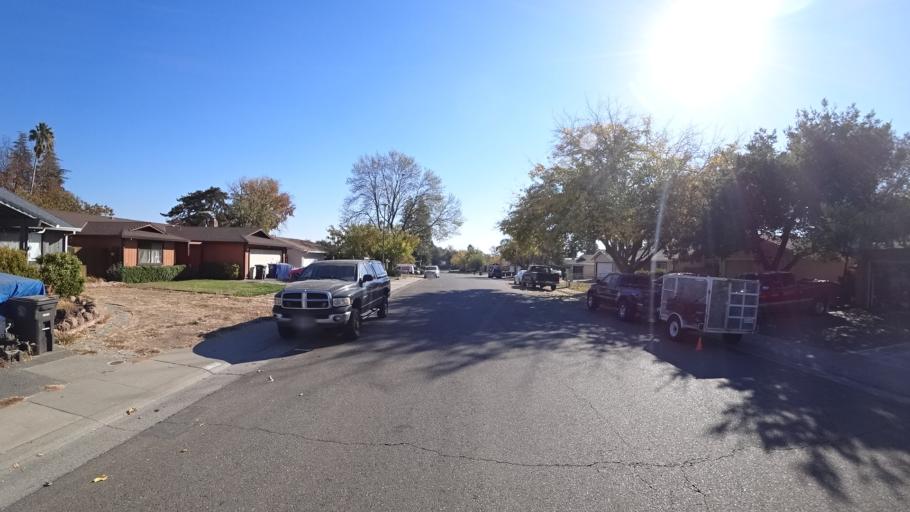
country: US
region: California
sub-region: Sacramento County
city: Antelope
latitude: 38.7127
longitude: -121.3143
